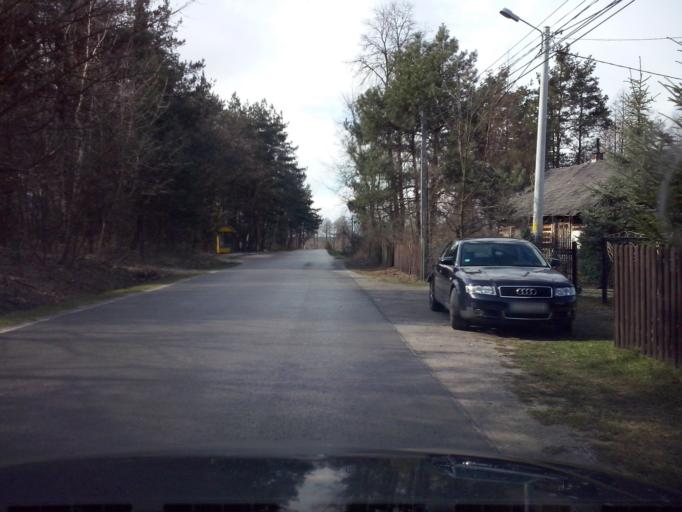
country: PL
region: Subcarpathian Voivodeship
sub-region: Powiat nizanski
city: Krzeszow
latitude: 50.4157
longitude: 22.3357
